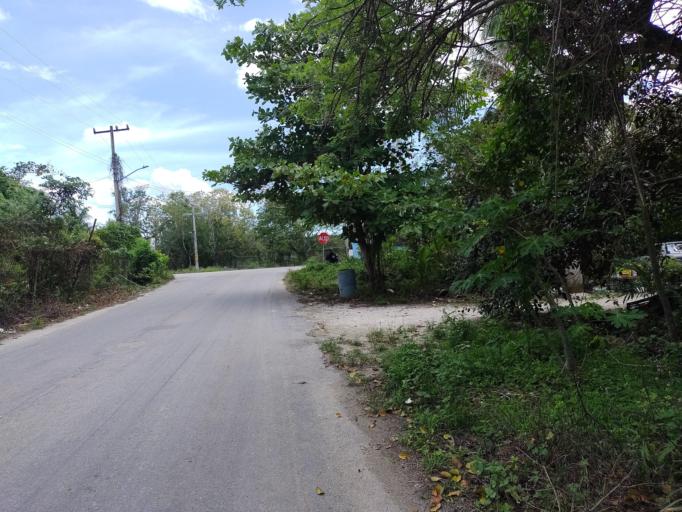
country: MX
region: Quintana Roo
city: San Miguel de Cozumel
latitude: 20.4824
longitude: -86.9136
